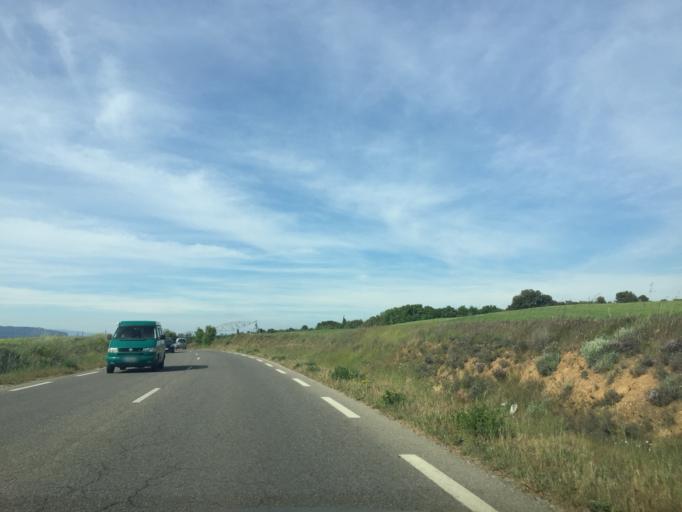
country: FR
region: Provence-Alpes-Cote d'Azur
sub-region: Departement du Var
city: Vinon-sur-Verdon
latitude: 43.7446
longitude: 5.8023
